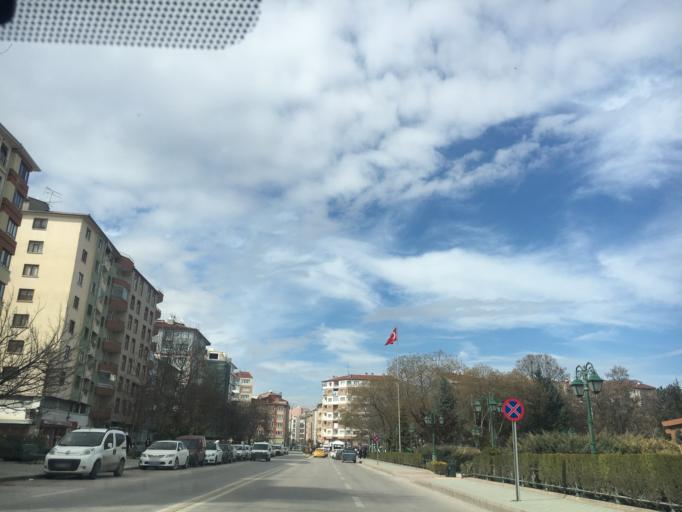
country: TR
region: Eskisehir
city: Eskisehir
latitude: 39.7808
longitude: 30.5272
